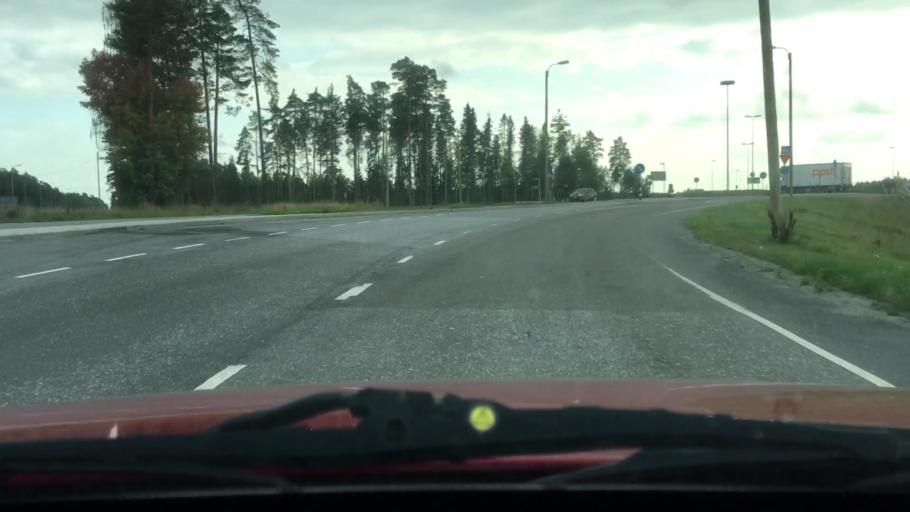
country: FI
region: Varsinais-Suomi
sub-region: Turku
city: Masku
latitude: 60.5433
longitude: 22.1291
